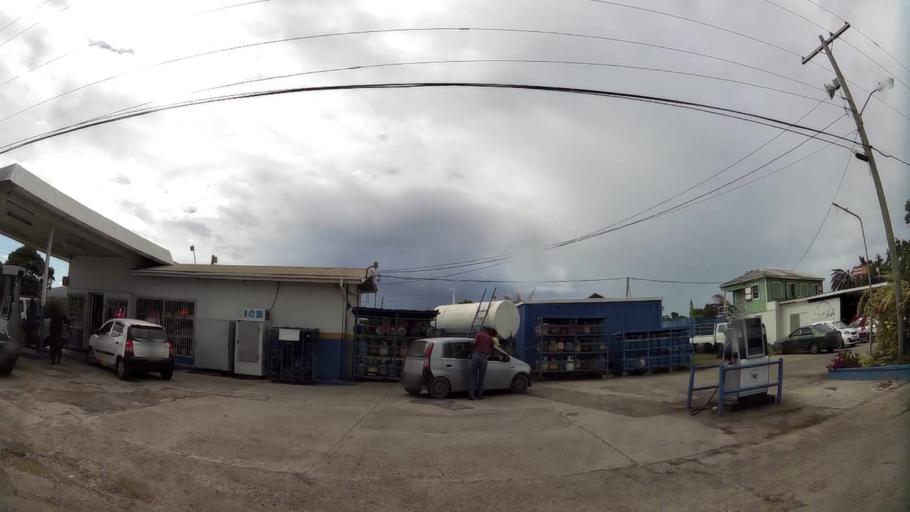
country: AG
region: Saint John
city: Potters Village
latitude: 17.0932
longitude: -61.8175
